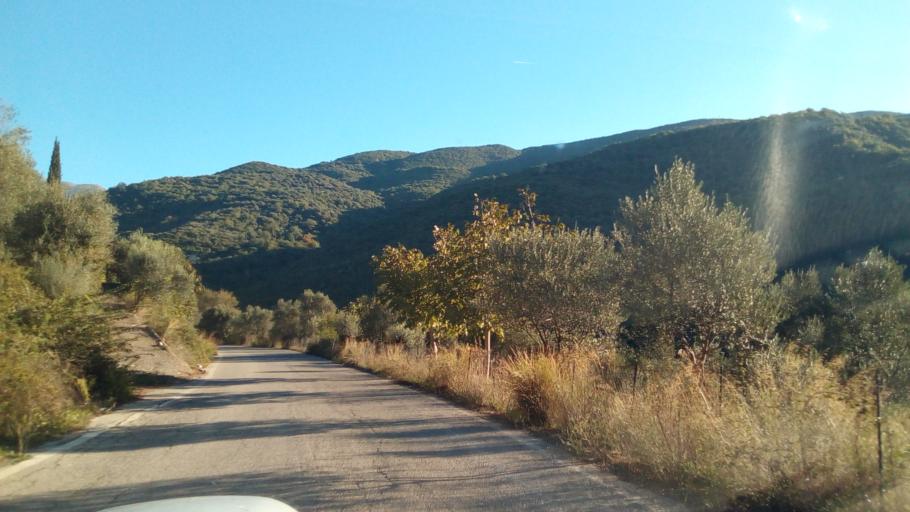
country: GR
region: West Greece
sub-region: Nomos Aitolias kai Akarnanias
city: Nafpaktos
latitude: 38.4427
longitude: 21.8834
